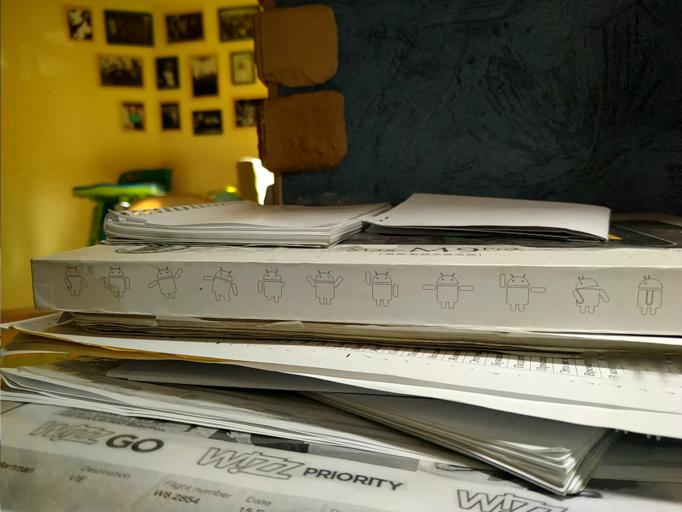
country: RU
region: Novgorod
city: Poddor'ye
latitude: 57.5118
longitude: 30.9295
